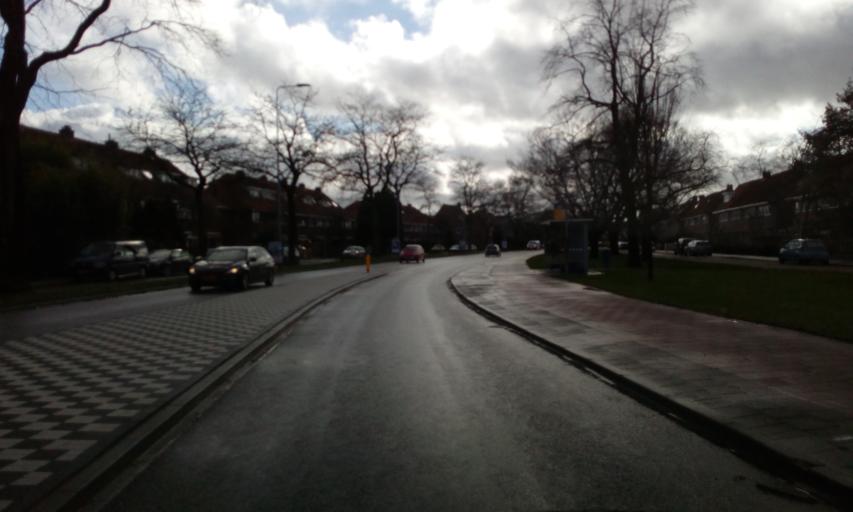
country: NL
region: North Holland
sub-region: Gemeente Hilversum
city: Hilversum
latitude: 52.2273
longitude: 5.1997
